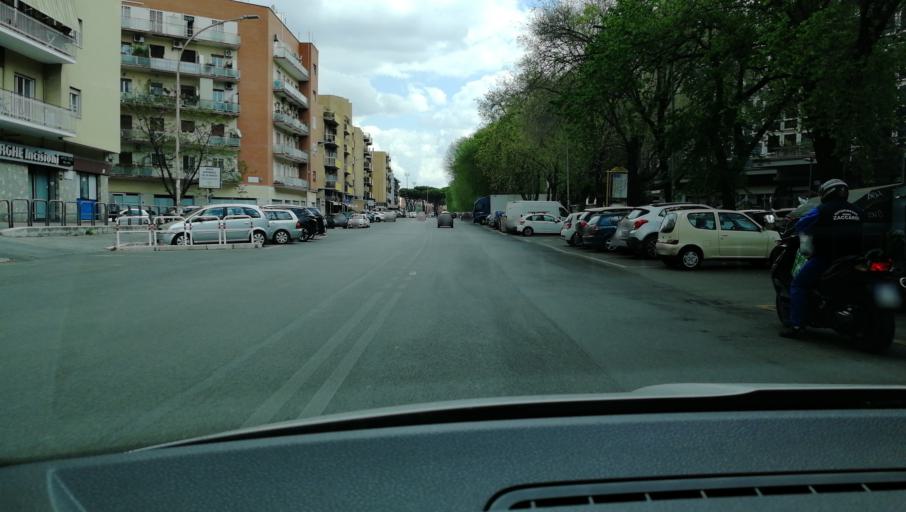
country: IT
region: Latium
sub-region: Citta metropolitana di Roma Capitale
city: Rome
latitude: 41.8510
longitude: 12.4939
